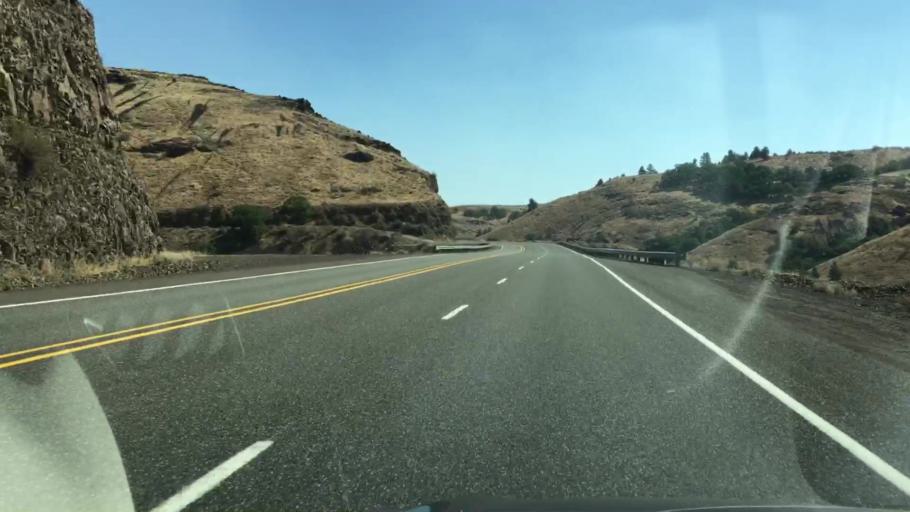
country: US
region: Oregon
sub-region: Wasco County
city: The Dalles
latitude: 45.3006
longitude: -121.1576
